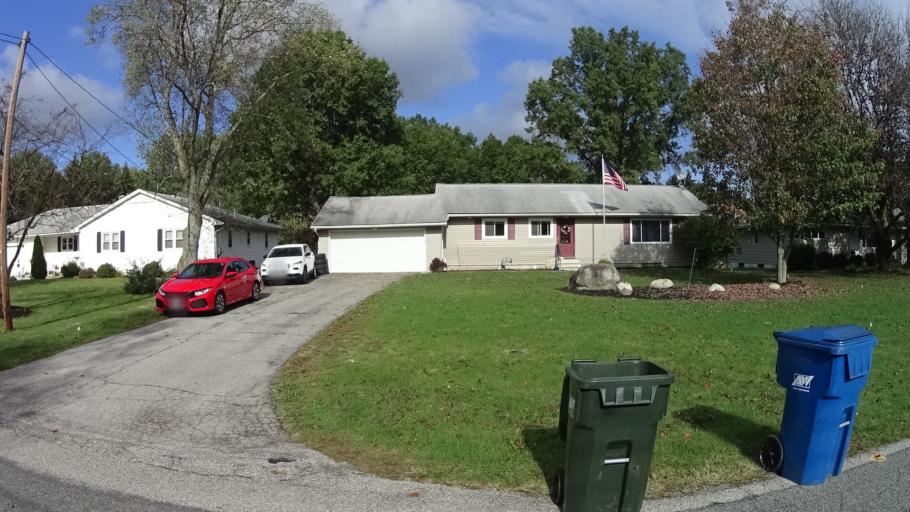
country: US
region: Ohio
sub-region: Lorain County
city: Grafton
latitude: 41.3245
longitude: -82.0725
